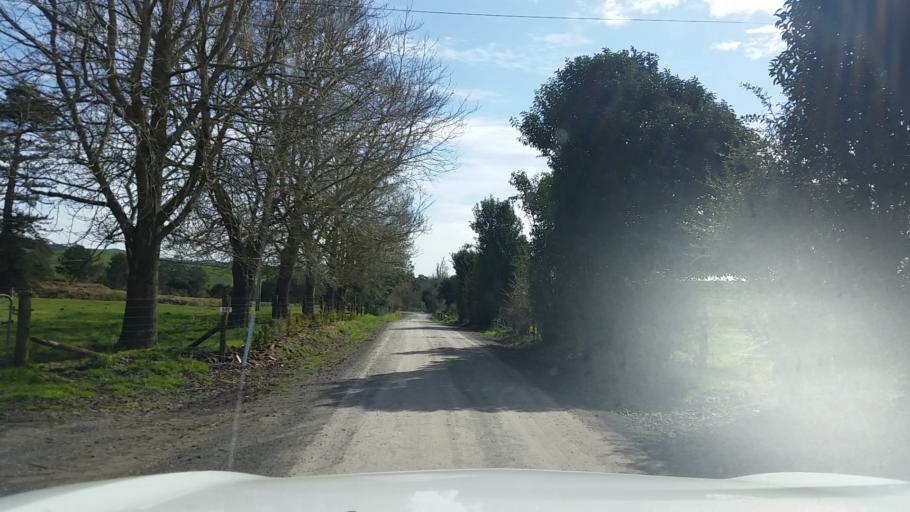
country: NZ
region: Waikato
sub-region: Hauraki District
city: Ngatea
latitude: -37.4458
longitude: 175.4885
